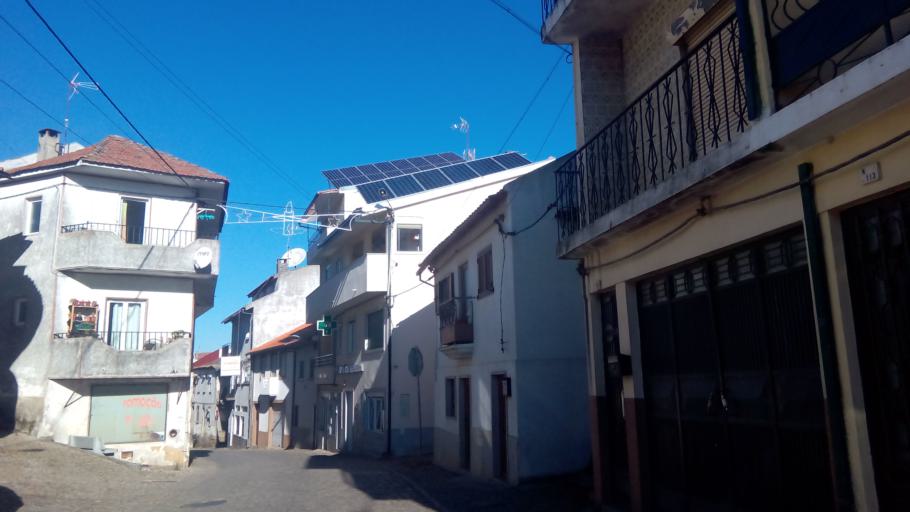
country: PT
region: Braganca
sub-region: Vimioso
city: Vimioso
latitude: 41.6410
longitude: -6.6010
